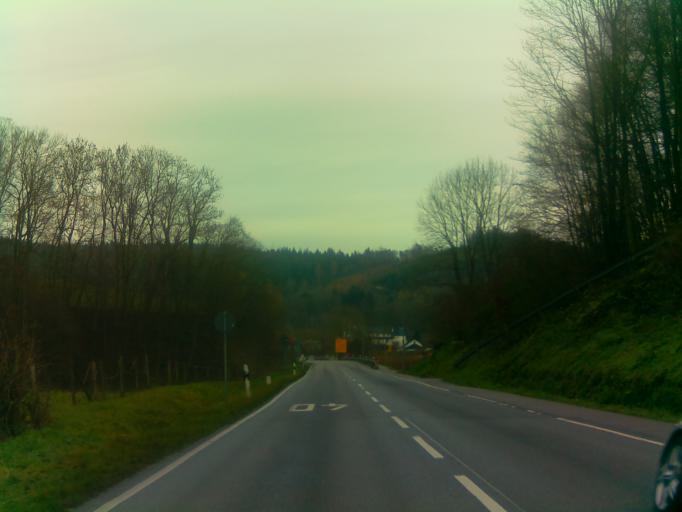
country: DE
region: Hesse
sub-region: Regierungsbezirk Darmstadt
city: Furth
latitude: 49.6608
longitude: 8.8345
